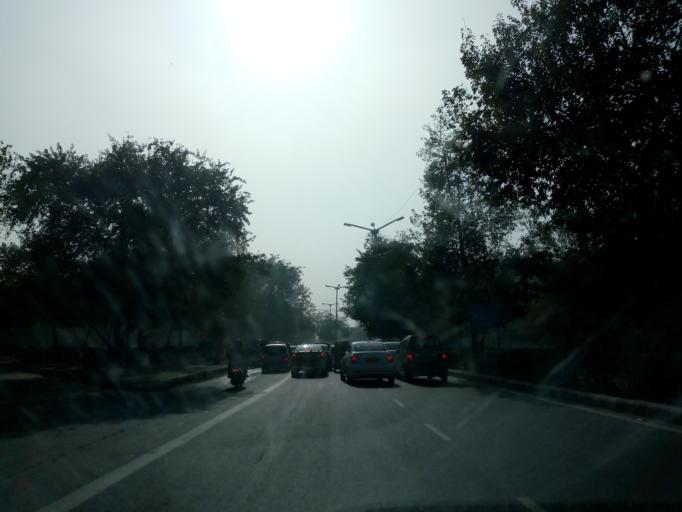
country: IN
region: NCT
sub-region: West Delhi
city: Nangloi Jat
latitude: 28.6022
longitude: 77.0427
